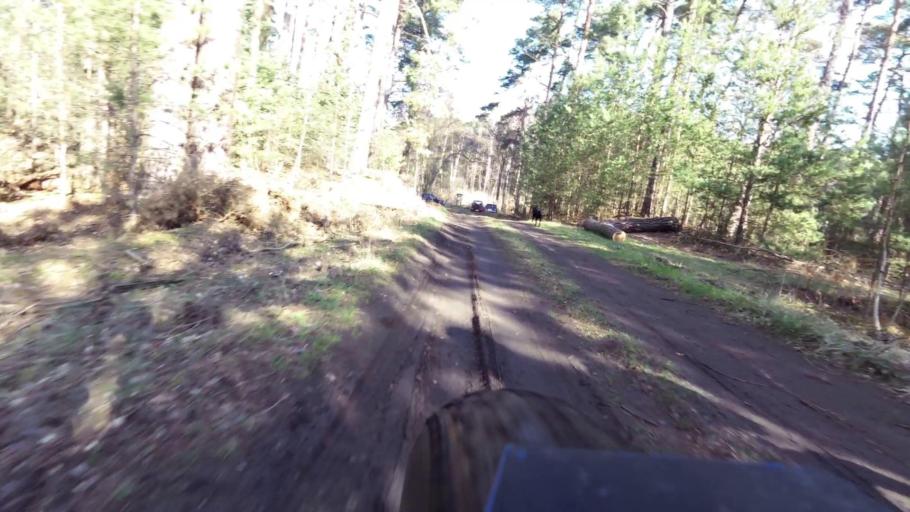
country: PL
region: Lubusz
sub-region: Powiat sulecinski
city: Torzym
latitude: 52.2207
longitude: 15.0051
